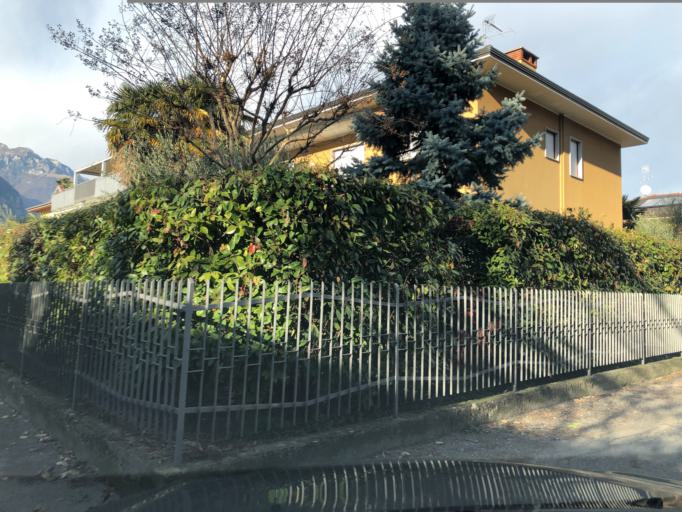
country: IT
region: Trentino-Alto Adige
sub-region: Provincia di Trento
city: Riva del Garda
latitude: 45.8902
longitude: 10.8612
